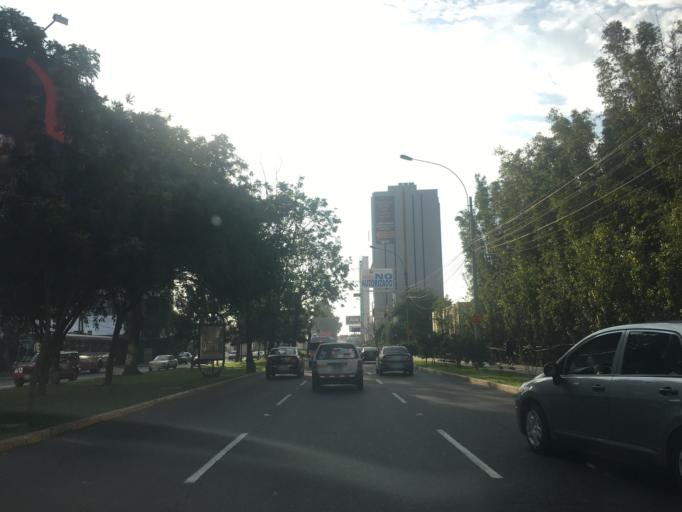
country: PE
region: Lima
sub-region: Lima
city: San Isidro
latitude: -12.0910
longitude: -77.0561
